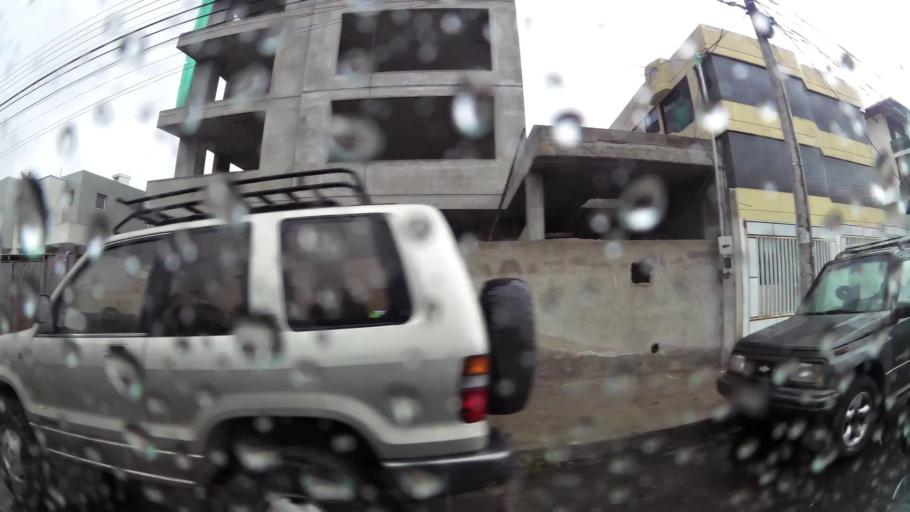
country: EC
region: Pichincha
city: Quito
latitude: -0.1006
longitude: -78.4995
